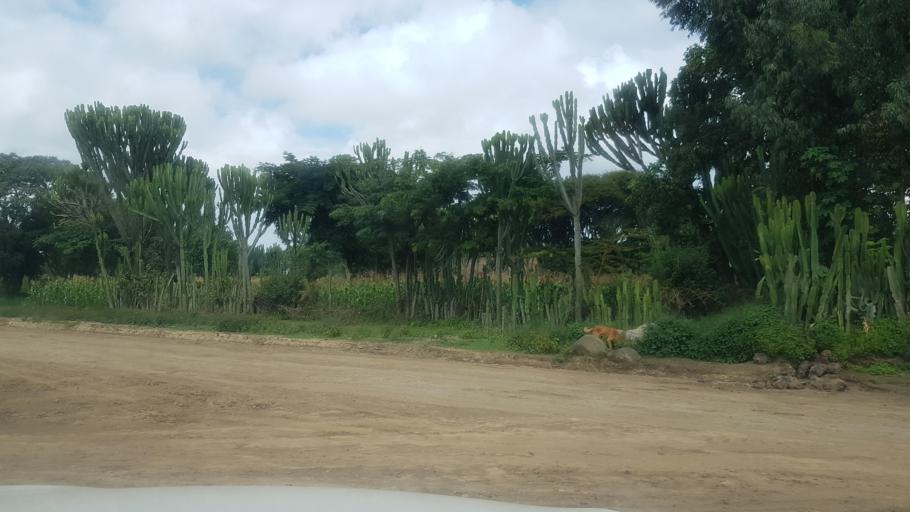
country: ET
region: Oromiya
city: Shashemene
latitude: 7.2629
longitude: 38.5961
